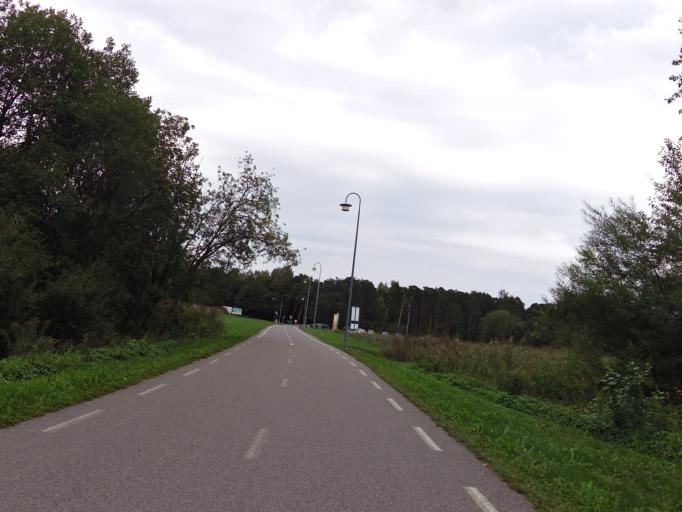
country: EE
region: Harju
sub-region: Tallinna linn
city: Tallinn
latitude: 59.4345
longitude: 24.6815
